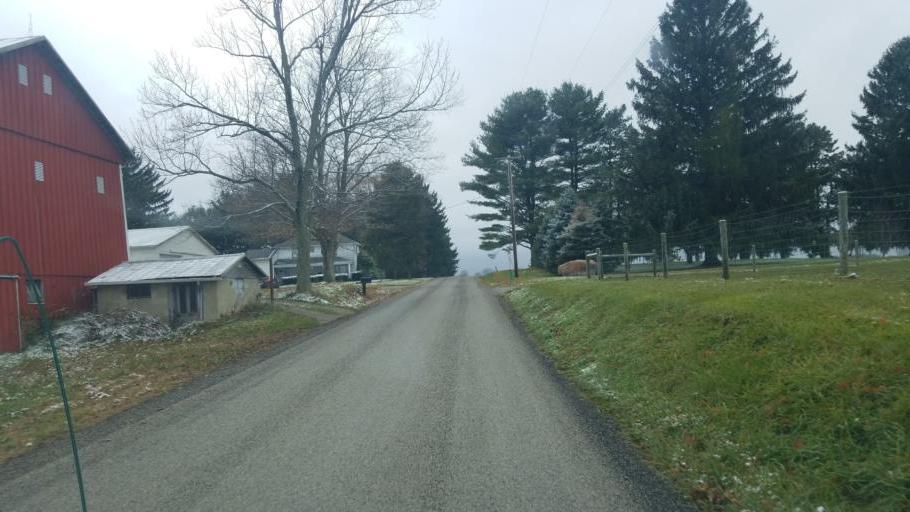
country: US
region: Ohio
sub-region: Richland County
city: Ontario
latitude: 40.8506
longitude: -82.5580
